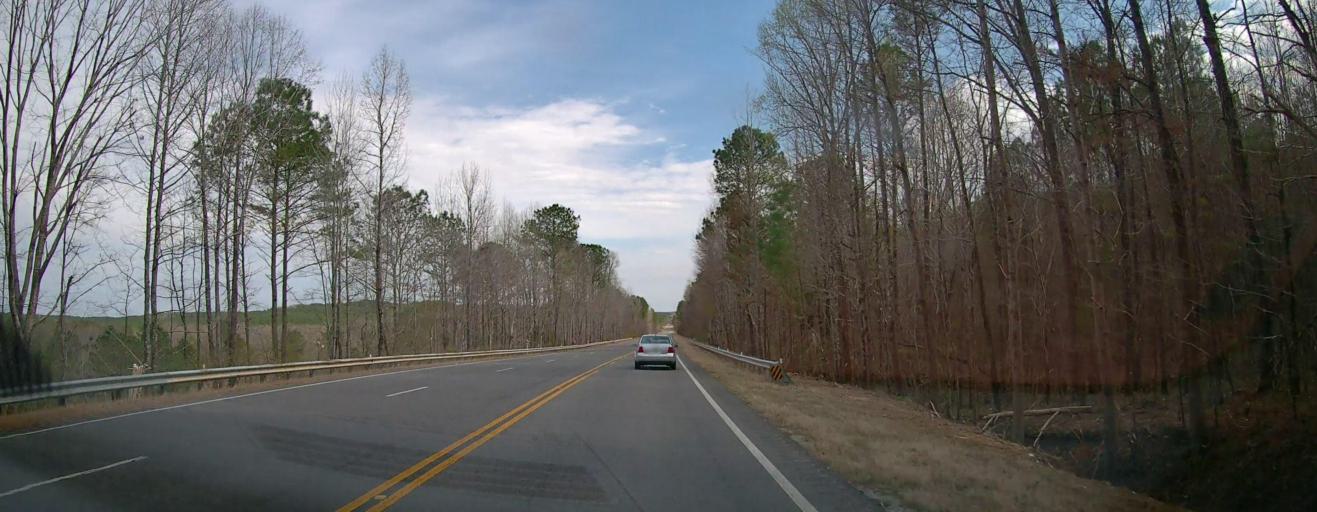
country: US
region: Alabama
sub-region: Walker County
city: Carbon Hill
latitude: 33.9155
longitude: -87.5658
